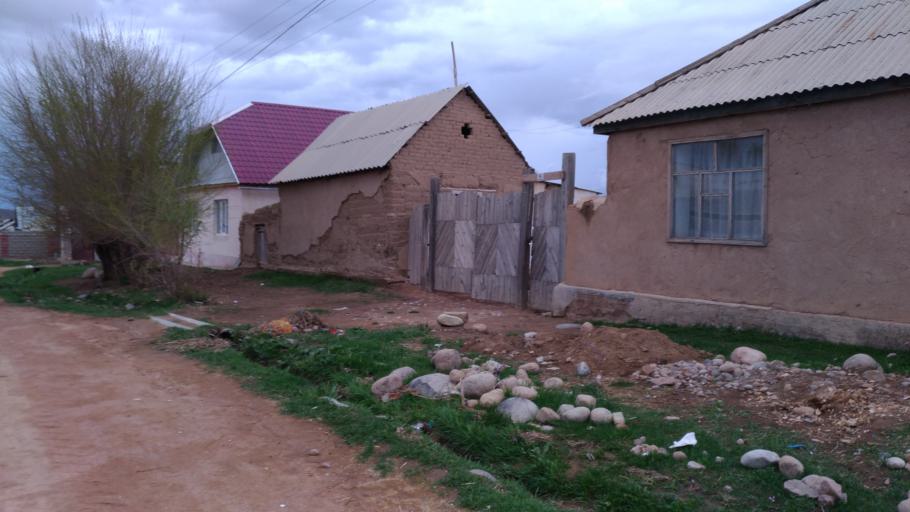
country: KG
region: Ysyk-Koel
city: Bokombayevskoye
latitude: 42.1082
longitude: 76.9823
